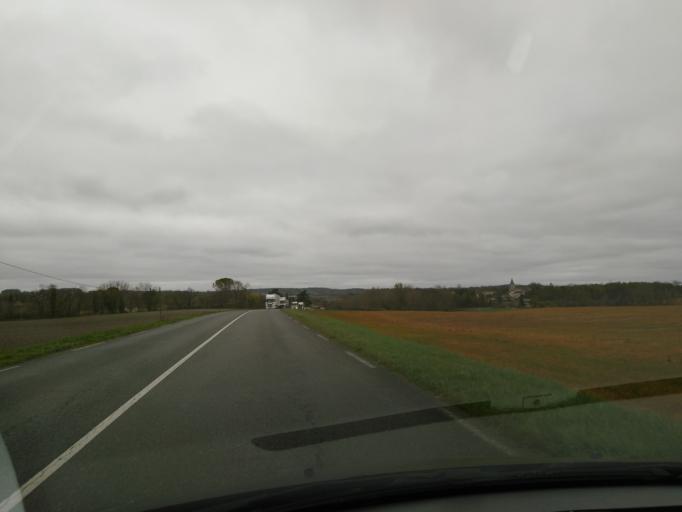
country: FR
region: Aquitaine
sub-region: Departement du Lot-et-Garonne
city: Castillonnes
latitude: 44.6945
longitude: 0.5670
